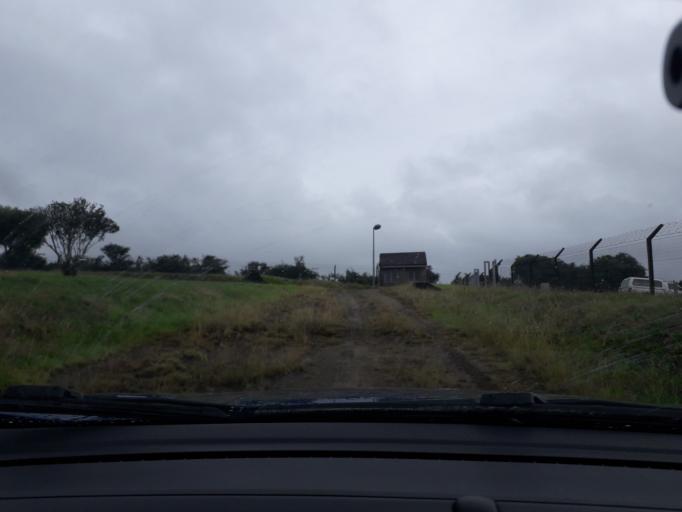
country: ZA
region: Eastern Cape
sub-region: Buffalo City Metropolitan Municipality
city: Bhisho
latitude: -32.7831
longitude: 27.3685
